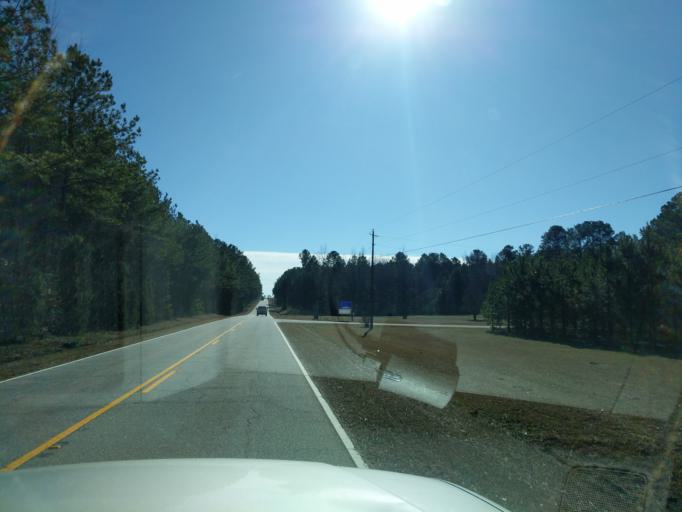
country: US
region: South Carolina
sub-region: Saluda County
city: Saluda
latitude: 34.1218
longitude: -81.8373
